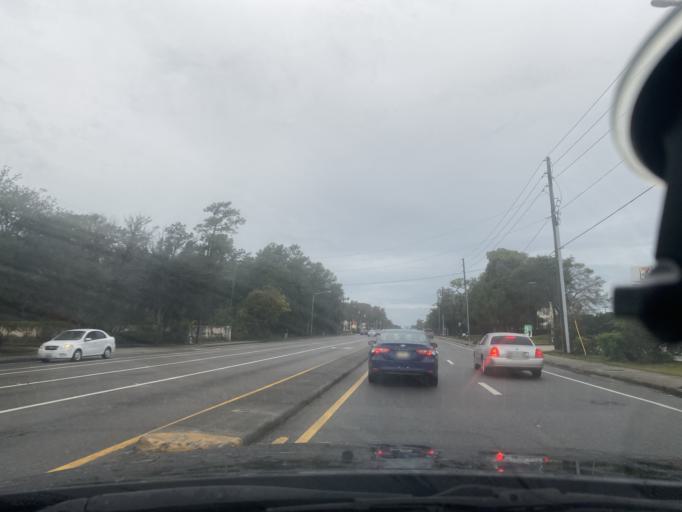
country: US
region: Florida
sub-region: Orange County
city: Azalea Park
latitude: 28.5393
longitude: -81.2768
